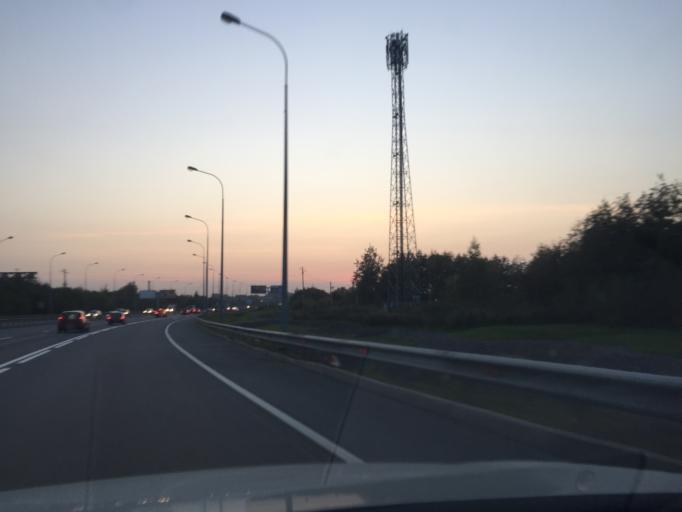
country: RU
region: St.-Petersburg
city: Krasnogvargeisky
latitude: 59.9887
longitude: 30.4779
